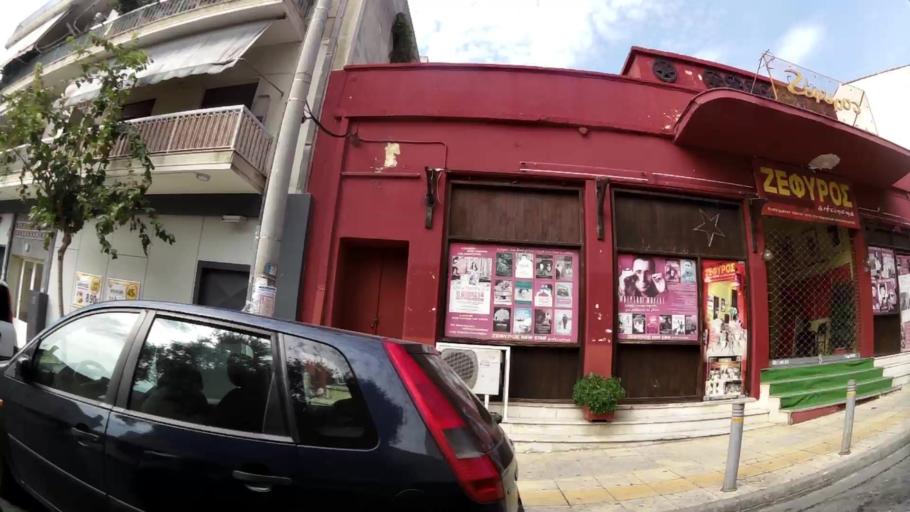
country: GR
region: Attica
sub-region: Nomarchia Athinas
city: Athens
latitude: 37.9696
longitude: 23.7130
